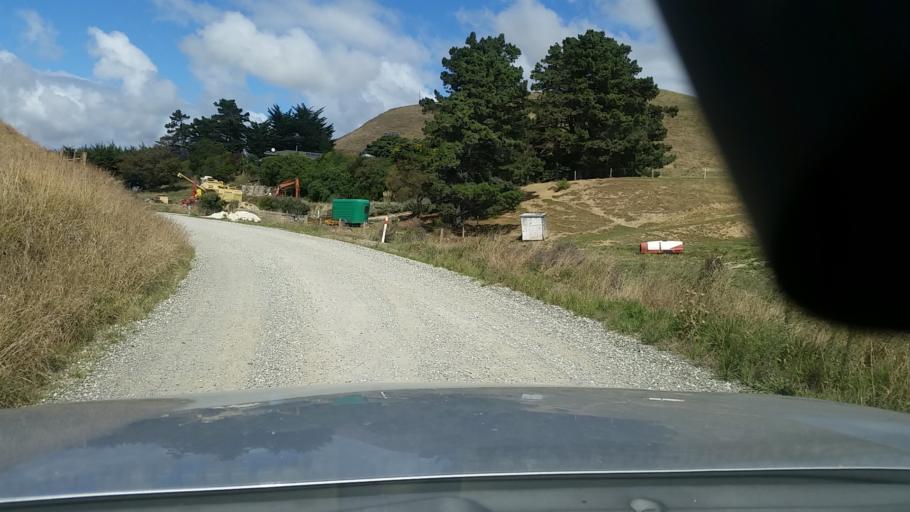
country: NZ
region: Marlborough
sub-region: Marlborough District
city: Blenheim
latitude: -41.7013
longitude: 174.1490
